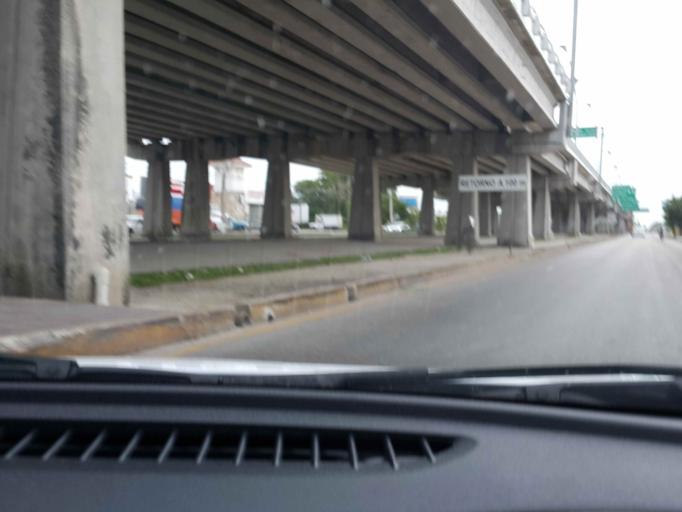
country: MX
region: Quintana Roo
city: Playa del Carmen
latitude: 20.6389
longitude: -87.0749
